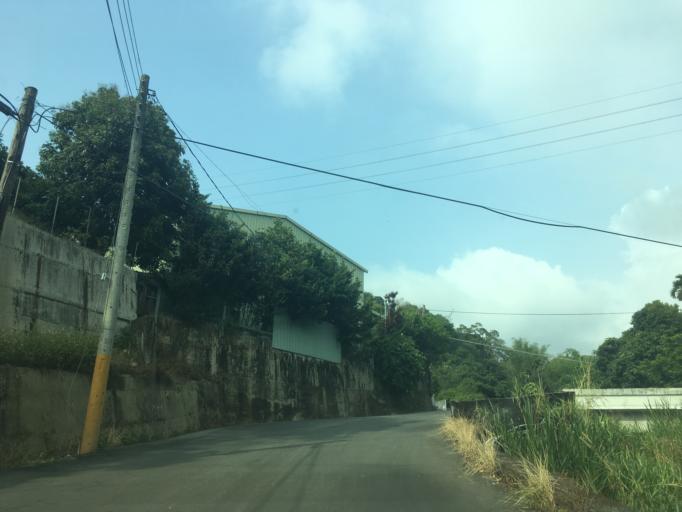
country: TW
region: Taiwan
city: Fengyuan
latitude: 24.2281
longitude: 120.7637
